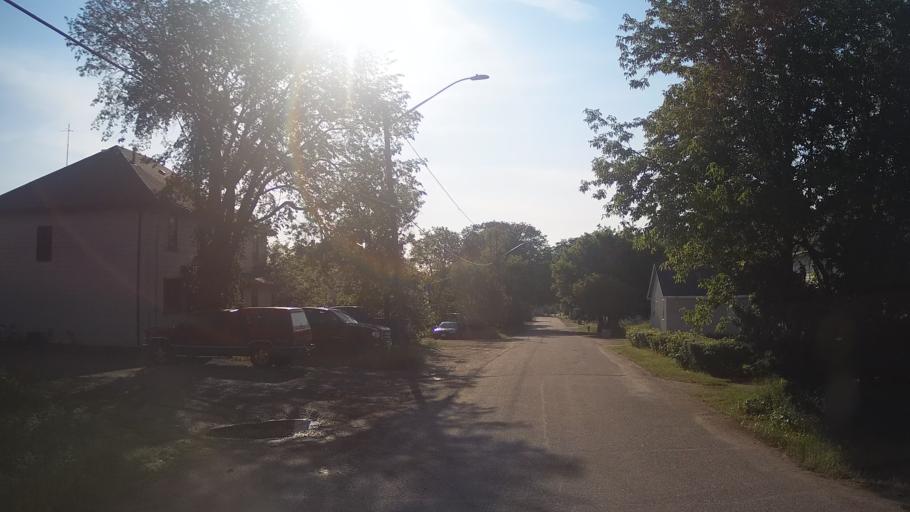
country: CA
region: Ontario
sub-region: Rainy River District
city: Atikokan
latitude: 49.4182
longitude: -91.6607
